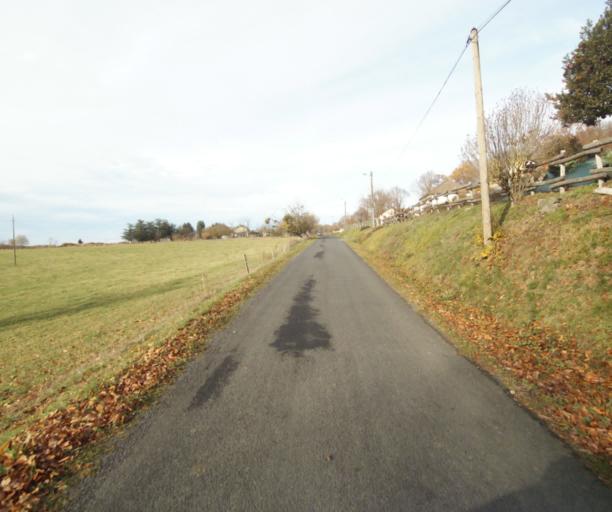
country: FR
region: Limousin
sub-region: Departement de la Correze
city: Sainte-Fortunade
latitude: 45.1724
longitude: 1.7426
